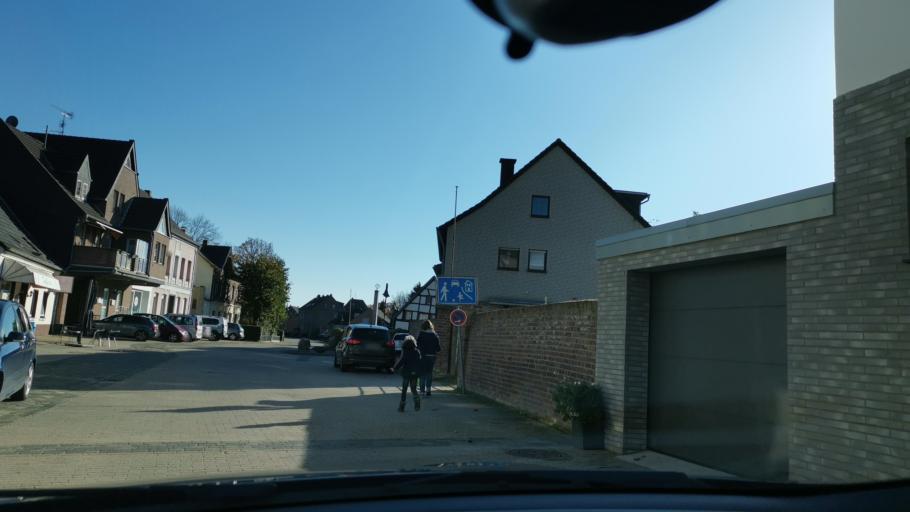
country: DE
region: North Rhine-Westphalia
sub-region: Regierungsbezirk Dusseldorf
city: Rommerskirchen
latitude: 51.0512
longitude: 6.7073
